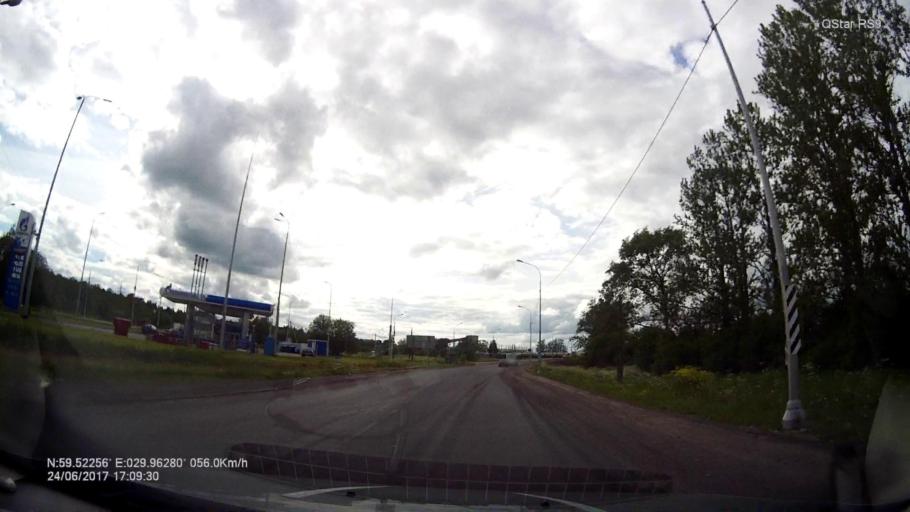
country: RU
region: Leningrad
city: Voyskovitsy
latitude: 59.5227
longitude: 29.9623
